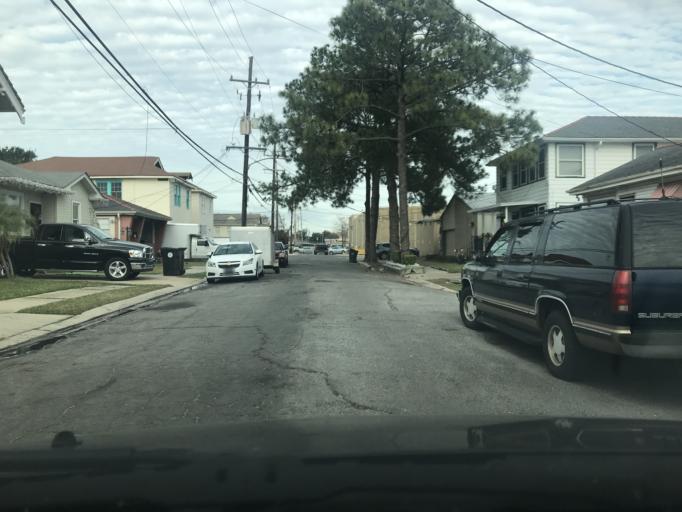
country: US
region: Louisiana
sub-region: Orleans Parish
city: New Orleans
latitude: 29.9531
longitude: -90.1037
